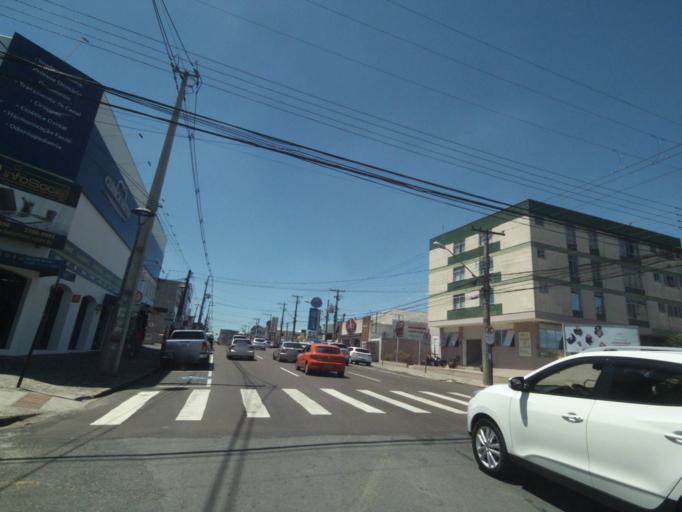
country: BR
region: Parana
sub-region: Curitiba
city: Curitiba
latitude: -25.4048
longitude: -49.2453
